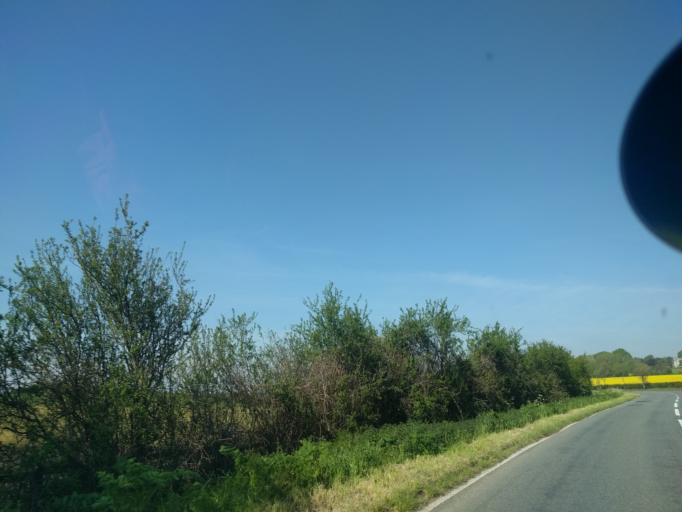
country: GB
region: England
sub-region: Somerset
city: Ilchester
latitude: 51.0261
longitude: -2.6803
